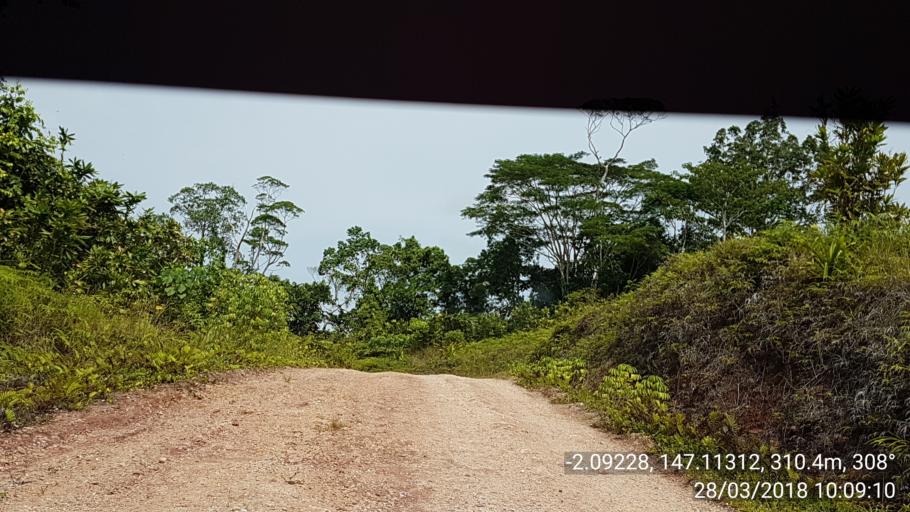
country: PG
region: Manus
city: Lorengau
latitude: -2.0922
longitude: 147.1131
